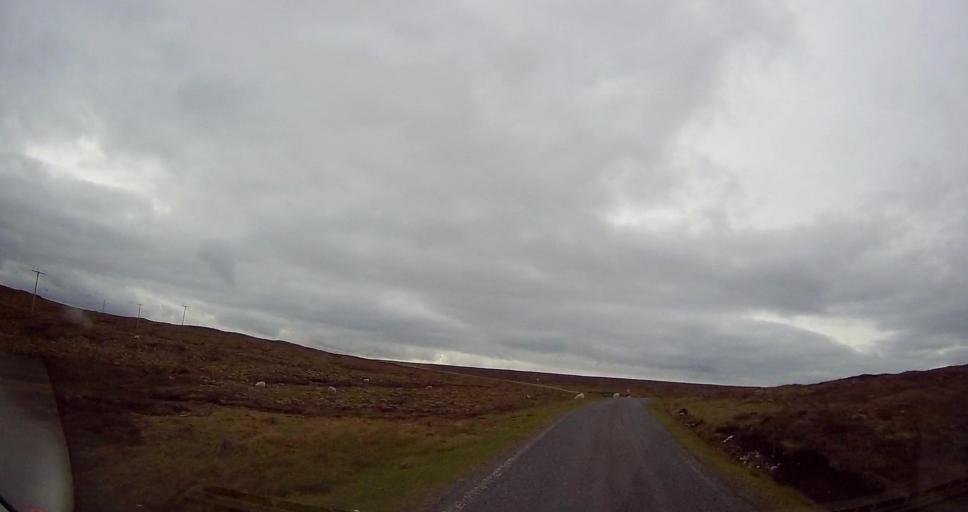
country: GB
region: Scotland
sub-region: Shetland Islands
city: Shetland
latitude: 60.5090
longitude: -1.1358
